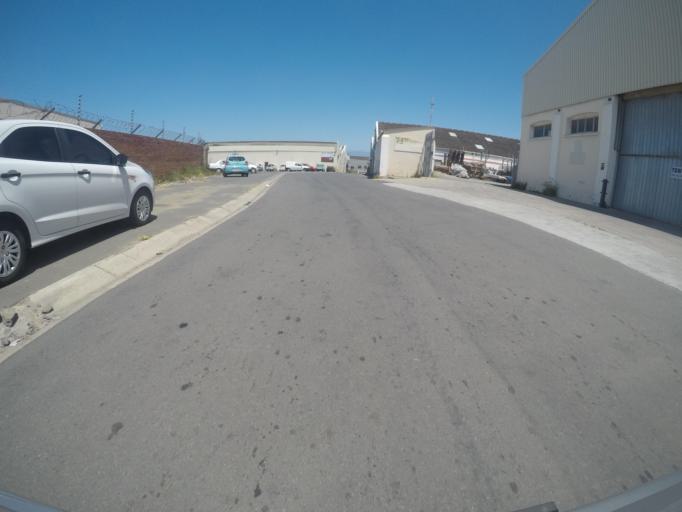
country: ZA
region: Eastern Cape
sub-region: Buffalo City Metropolitan Municipality
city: East London
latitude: -33.0094
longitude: 27.9149
